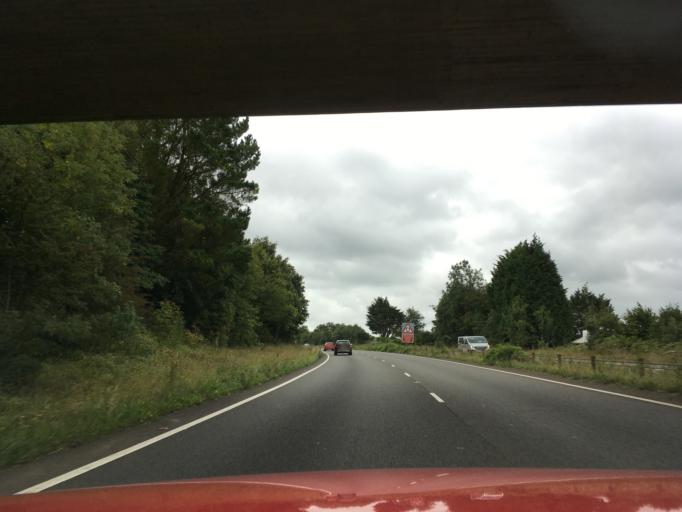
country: GB
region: England
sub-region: Devon
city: Kingskerswell
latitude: 50.4778
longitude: -3.5826
